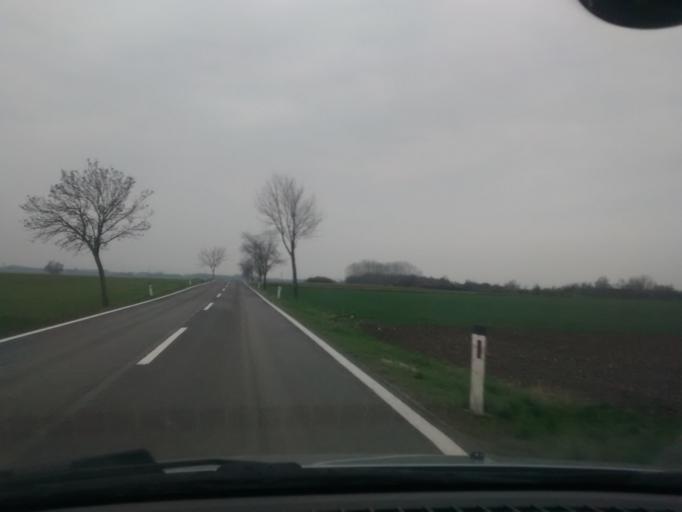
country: AT
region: Lower Austria
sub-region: Politischer Bezirk Wien-Umgebung
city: Moosbrunn
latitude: 48.0179
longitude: 16.4419
